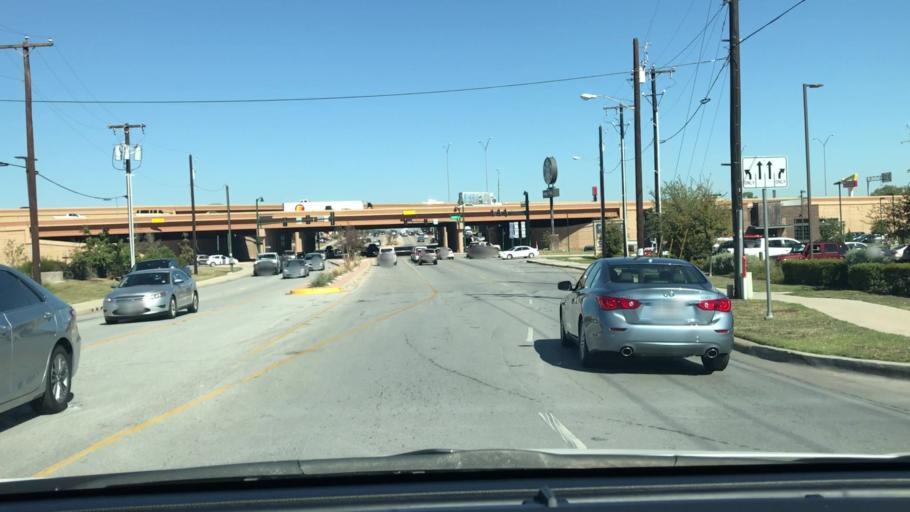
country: US
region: Texas
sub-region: Tarrant County
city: Hurst
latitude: 32.8376
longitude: -97.1863
